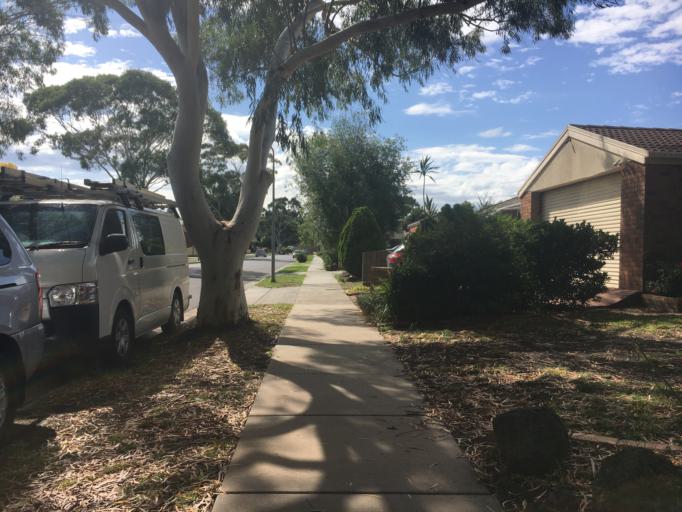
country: AU
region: Victoria
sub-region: Knox
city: Ferntree Gully
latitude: -37.8924
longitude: 145.2767
